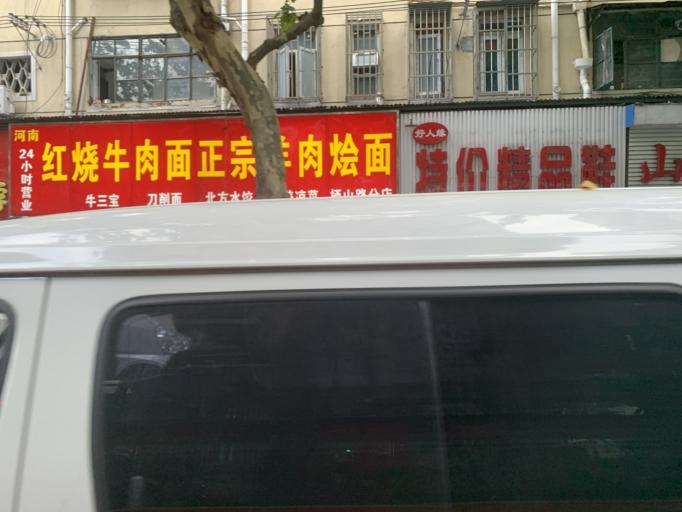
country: CN
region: Shanghai Shi
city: Pudong
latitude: 31.2488
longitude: 121.5465
